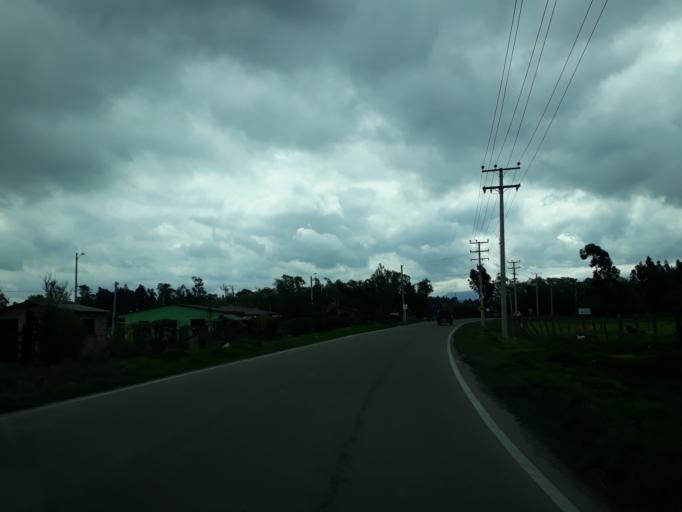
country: CO
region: Cundinamarca
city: Ubate
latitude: 5.3204
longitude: -73.7964
